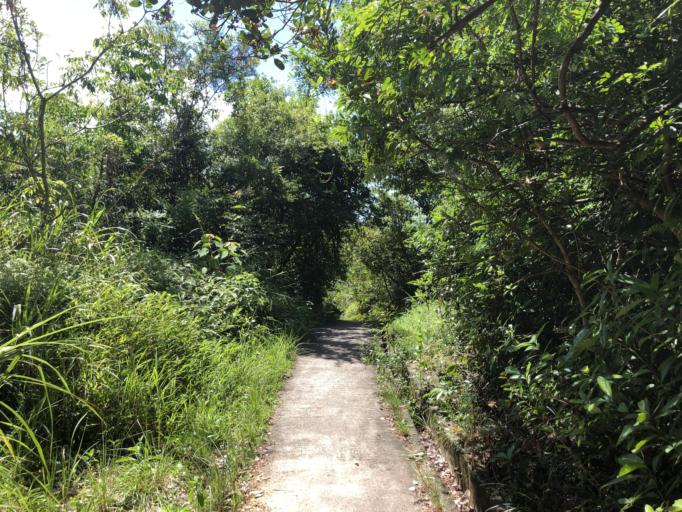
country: HK
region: Tuen Mun
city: Tuen Mun
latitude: 22.2889
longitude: 113.9800
